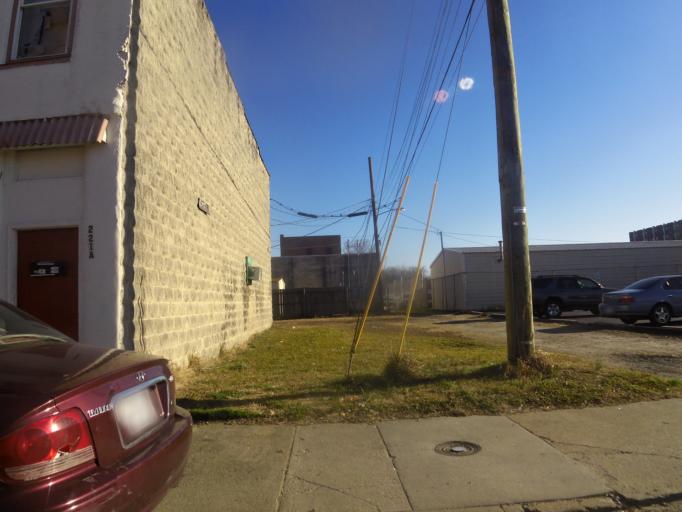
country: US
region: Virginia
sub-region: City of Hopewell
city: Hopewell
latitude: 37.3050
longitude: -77.2841
